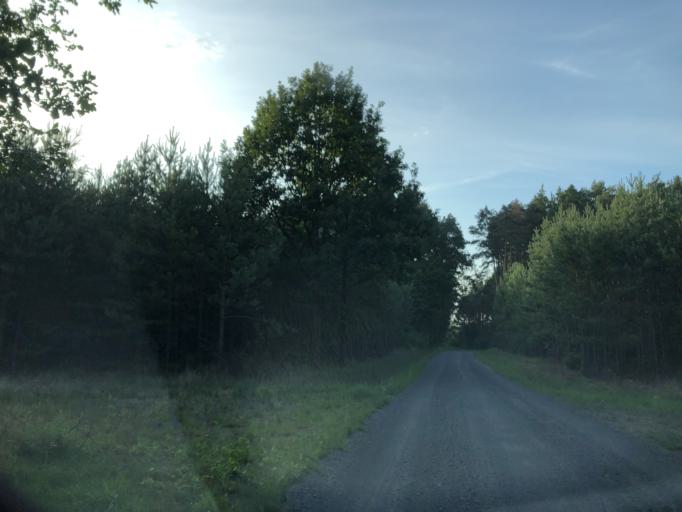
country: PL
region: Lubusz
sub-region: Powiat swiebodzinski
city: Zbaszynek
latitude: 52.2327
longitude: 15.7918
